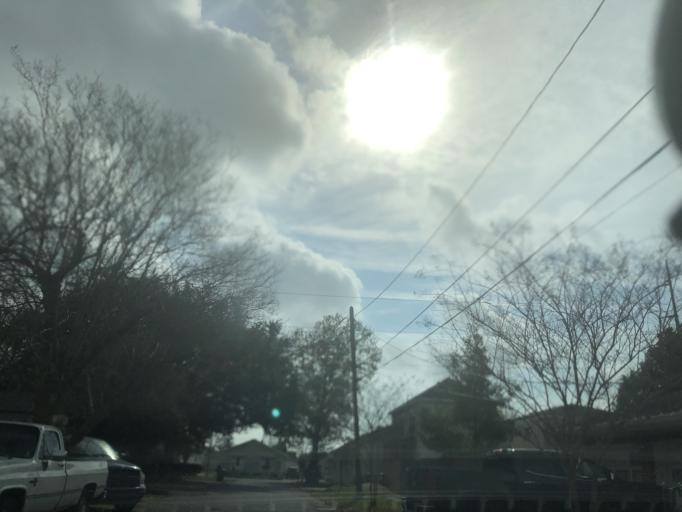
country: US
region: Louisiana
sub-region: Jefferson Parish
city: Metairie Terrace
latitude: 29.9775
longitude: -90.1645
